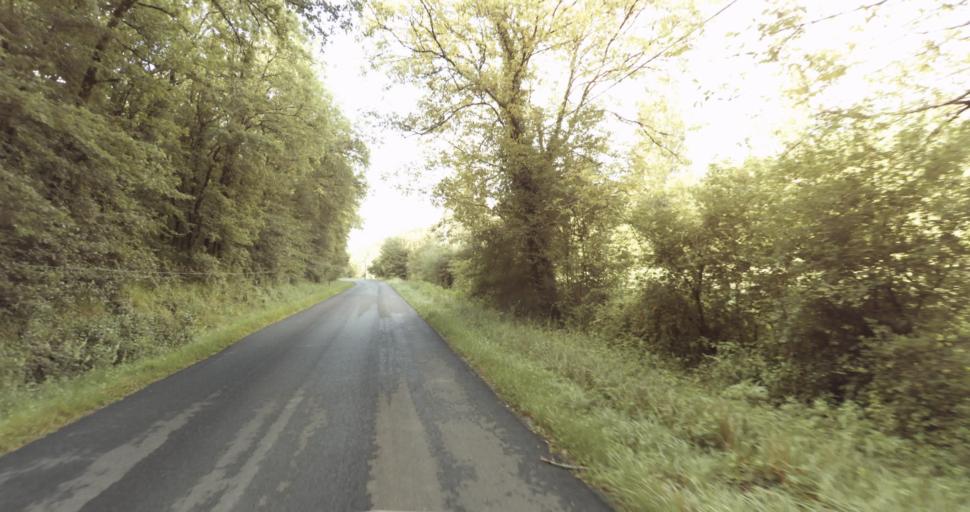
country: FR
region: Aquitaine
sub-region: Departement de la Dordogne
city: Lalinde
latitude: 44.8587
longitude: 0.7747
